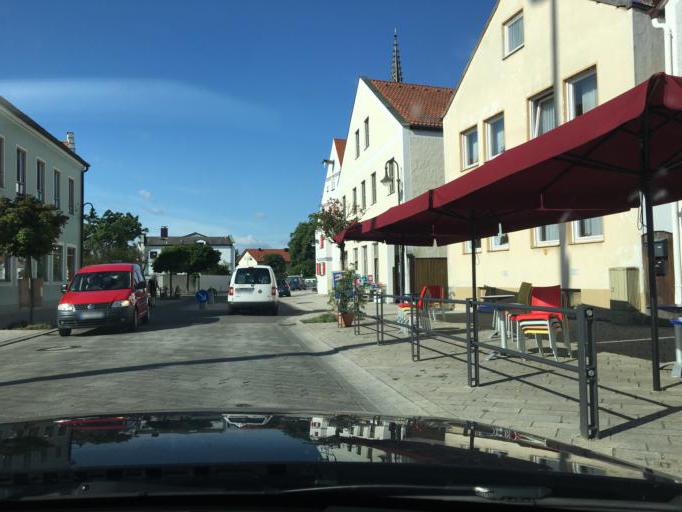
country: DE
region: Bavaria
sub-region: Upper Bavaria
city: Gaimersheim
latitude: 48.8081
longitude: 11.3697
